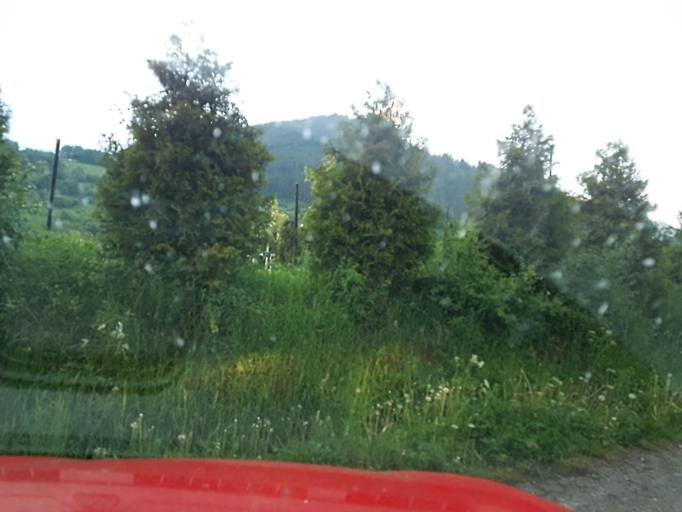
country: SK
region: Zilinsky
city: Ruzomberok
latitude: 49.1269
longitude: 19.4170
